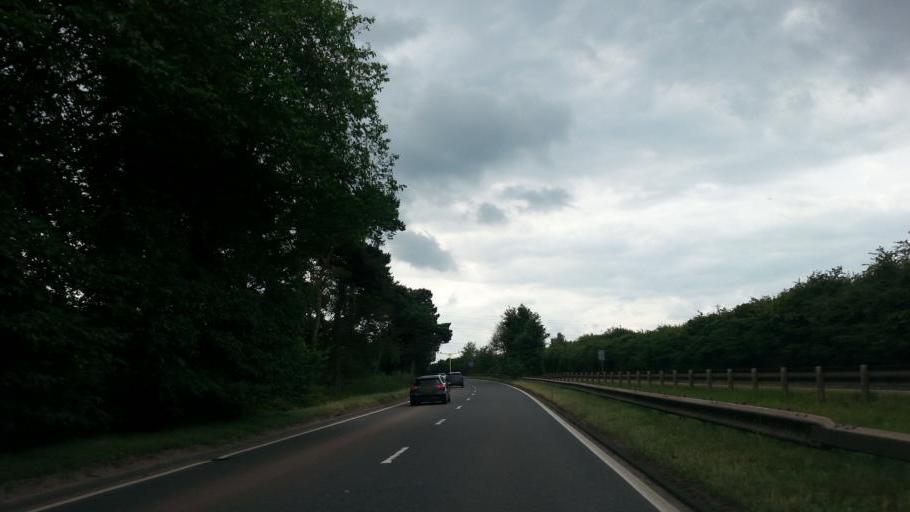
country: GB
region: England
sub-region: Staffordshire
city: Shenstone
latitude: 52.6178
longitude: -1.7984
